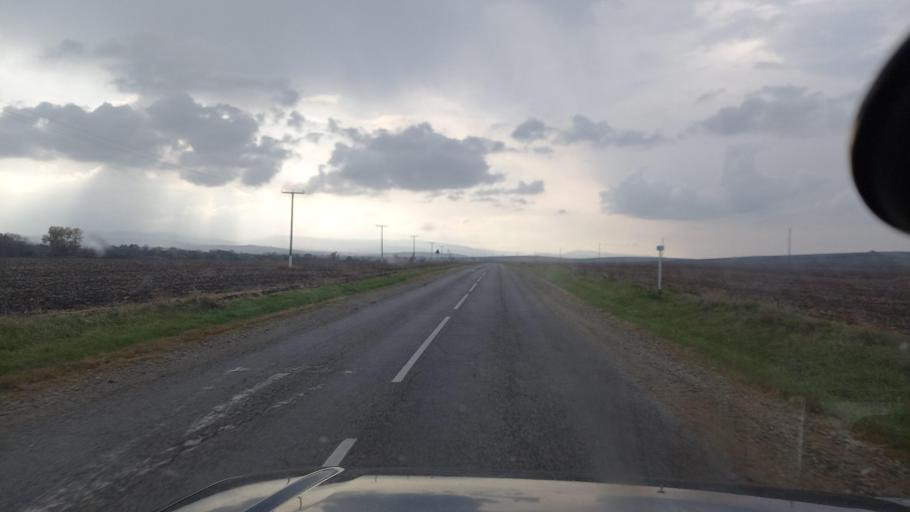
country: RU
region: Krasnodarskiy
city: Gubskaya
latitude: 44.3496
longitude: 40.6936
